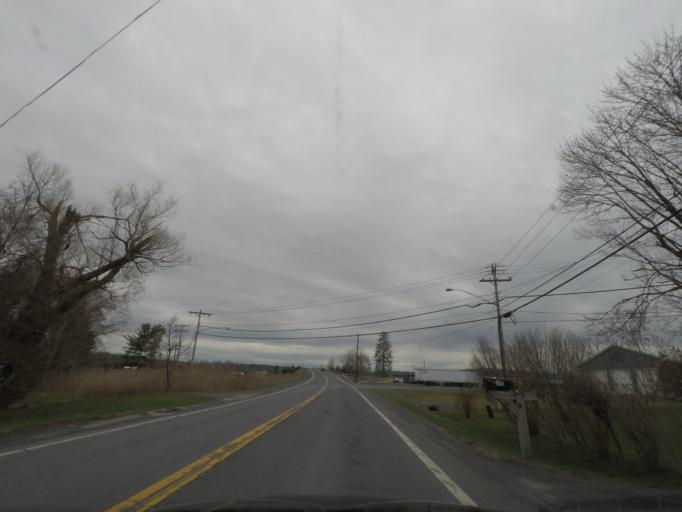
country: US
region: New York
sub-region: Rensselaer County
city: Castleton-on-Hudson
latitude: 42.5451
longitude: -73.8144
